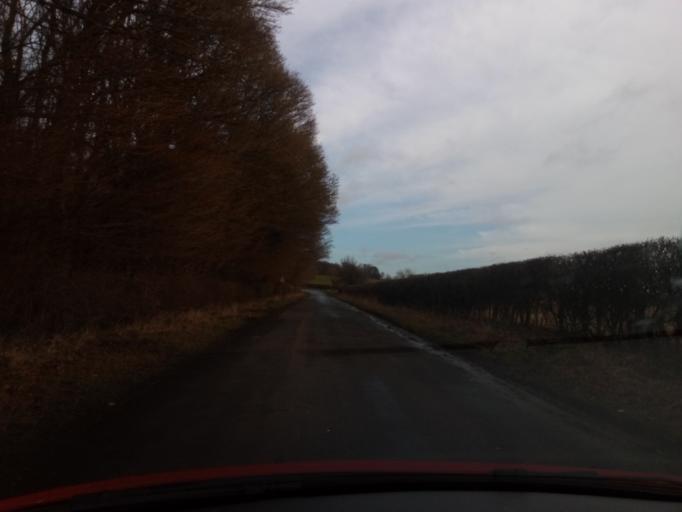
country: GB
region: England
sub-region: Northumberland
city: Corbridge
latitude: 54.9878
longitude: -2.0374
